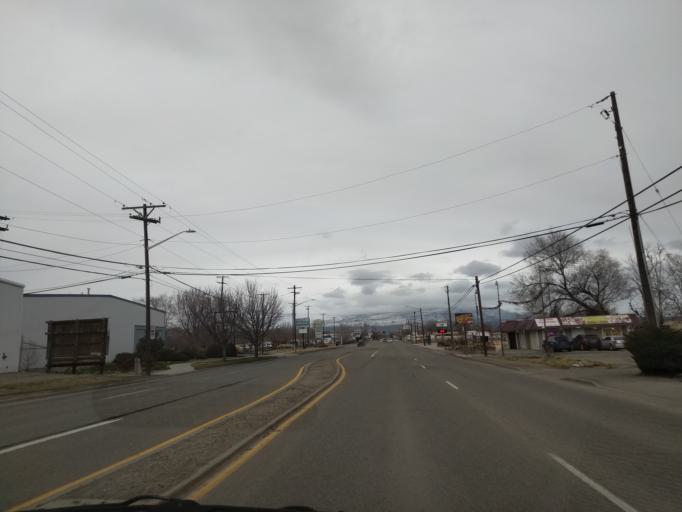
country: US
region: Colorado
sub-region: Mesa County
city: Fruitvale
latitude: 39.0773
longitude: -108.5104
